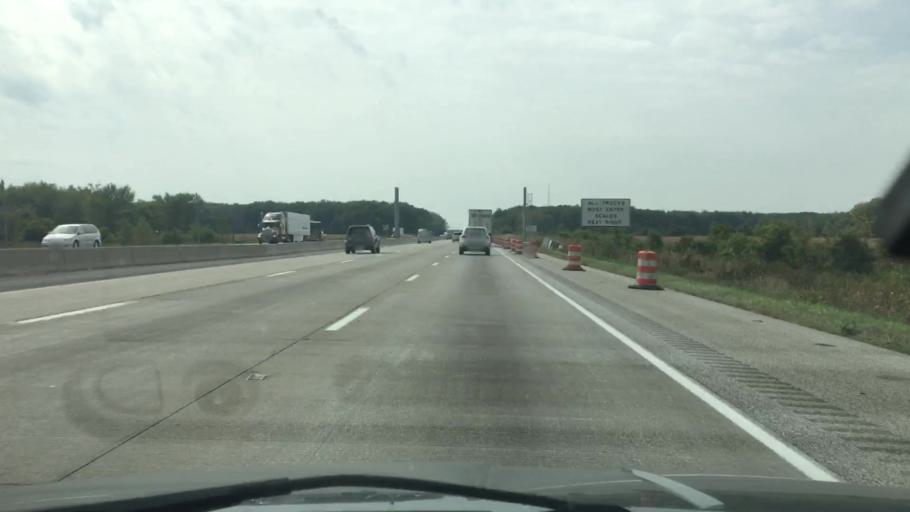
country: US
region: Indiana
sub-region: Porter County
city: Chesterton
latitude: 41.6512
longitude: -86.9797
